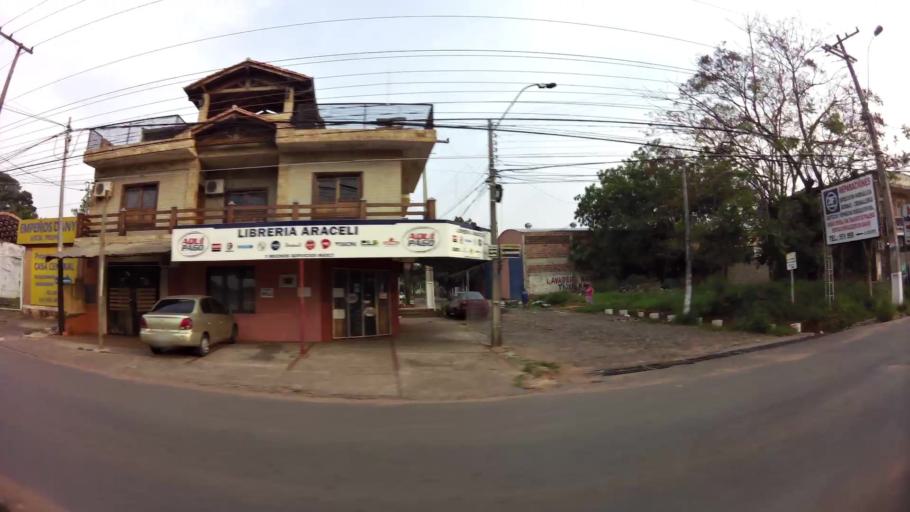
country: PY
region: Central
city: Lambare
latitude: -25.3389
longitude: -57.5905
